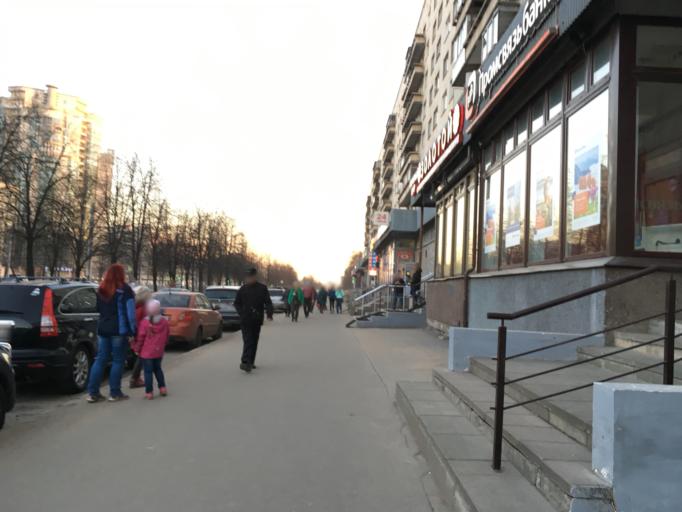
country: RU
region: St.-Petersburg
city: Grazhdanka
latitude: 60.0335
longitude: 30.4173
